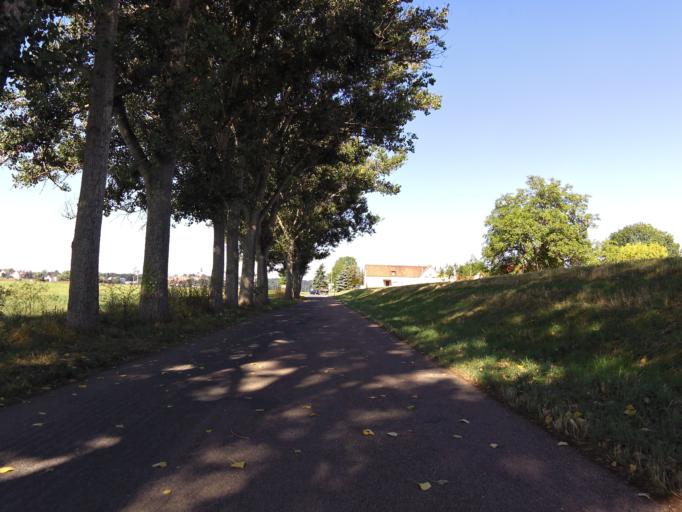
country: DE
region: Saxony
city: Strehla
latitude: 51.3517
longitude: 13.2524
